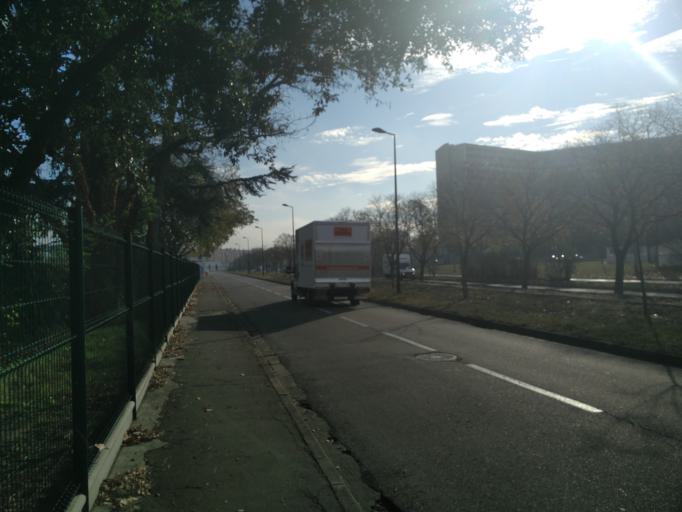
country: FR
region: Midi-Pyrenees
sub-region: Departement de la Haute-Garonne
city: Toulouse
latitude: 43.5738
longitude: 1.4063
